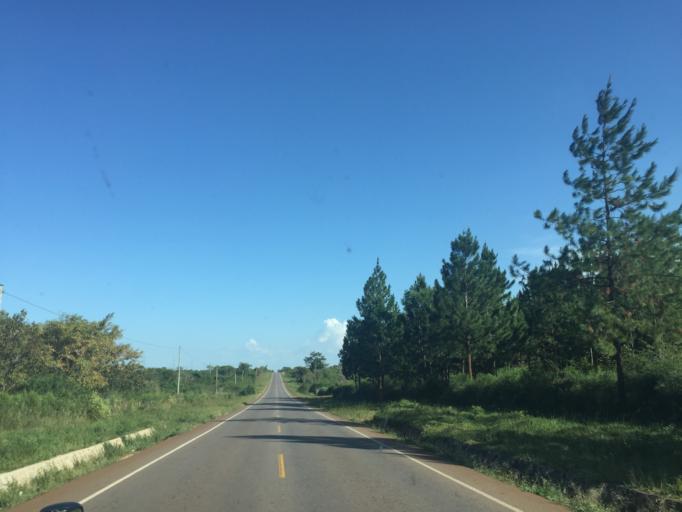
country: UG
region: Central Region
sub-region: Nakasongola District
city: Nakasongola
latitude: 1.3724
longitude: 32.3507
